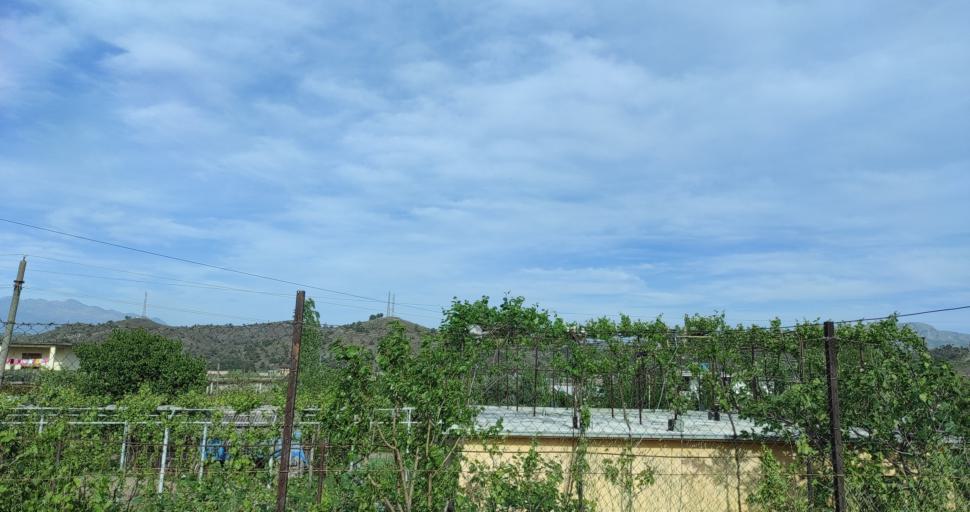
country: AL
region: Shkoder
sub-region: Rrethi i Shkodres
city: Shkoder
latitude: 42.0634
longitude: 19.5280
